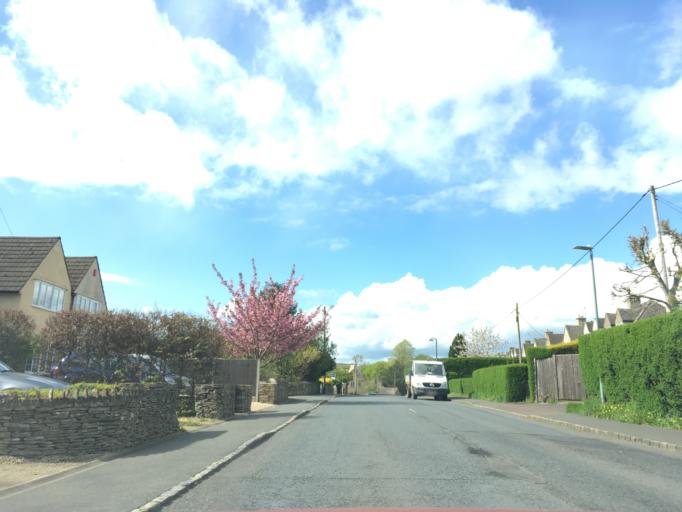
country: GB
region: England
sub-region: Gloucestershire
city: Tetbury
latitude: 51.6438
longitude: -2.1648
